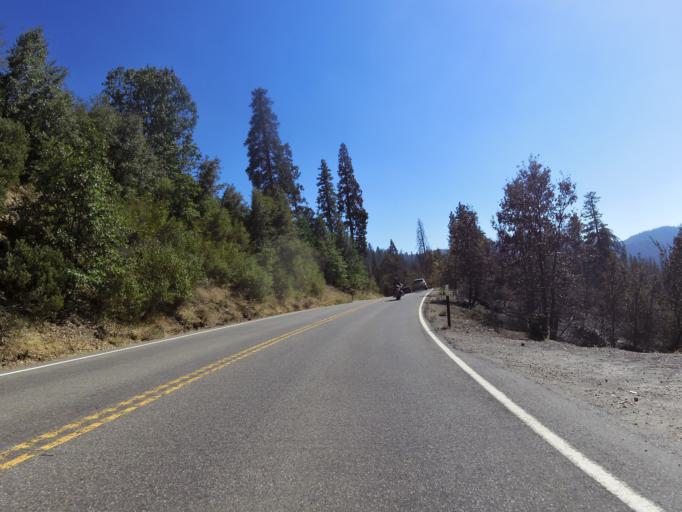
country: US
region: California
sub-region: Mariposa County
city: Yosemite Valley
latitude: 37.6954
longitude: -119.7077
